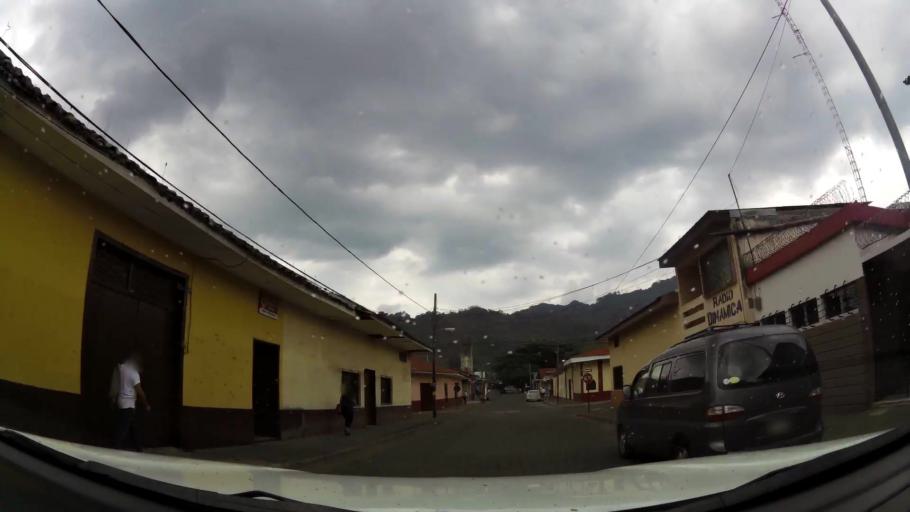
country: NI
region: Jinotega
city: Jinotega
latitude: 13.0897
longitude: -86.0013
